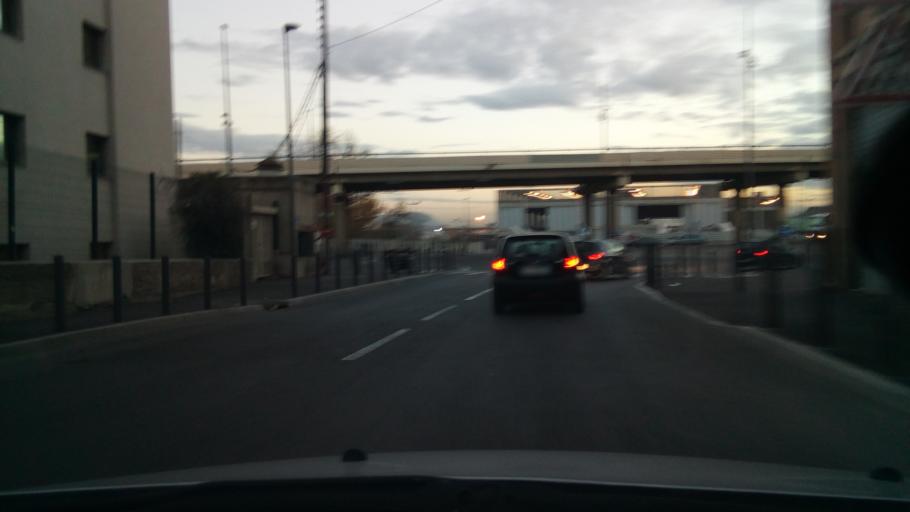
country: FR
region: Provence-Alpes-Cote d'Azur
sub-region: Departement des Bouches-du-Rhone
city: Marseille 14
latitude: 43.3299
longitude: 5.3666
